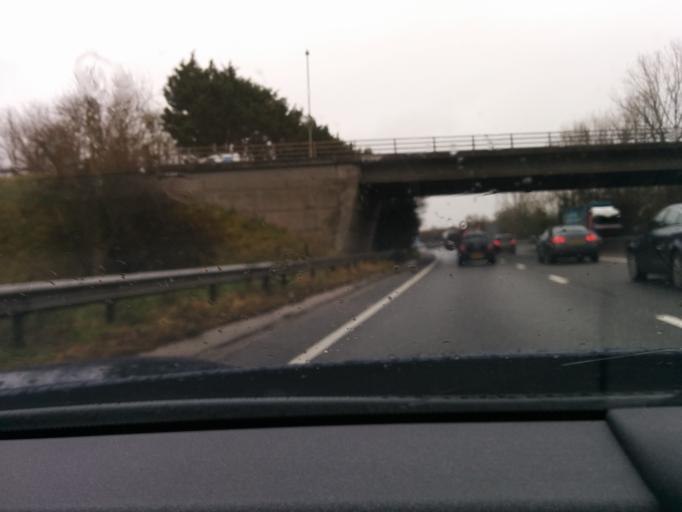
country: GB
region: England
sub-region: Oxfordshire
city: Abingdon
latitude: 51.6779
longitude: -1.3014
